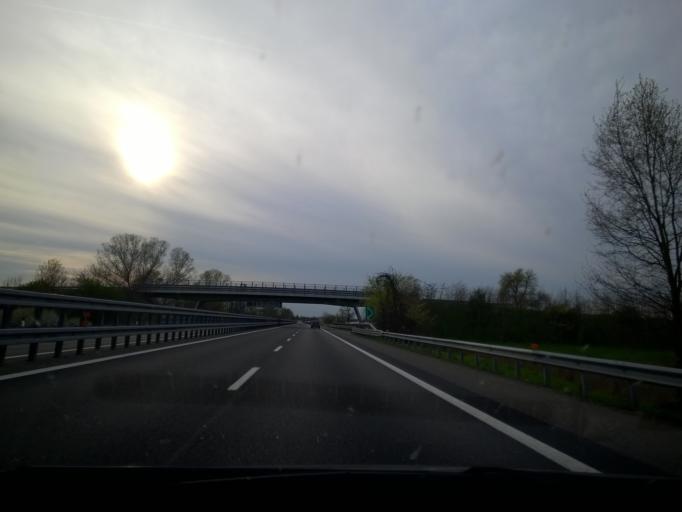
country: IT
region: Lombardy
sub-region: Provincia di Pavia
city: Zerbo
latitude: 45.0817
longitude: 9.4091
